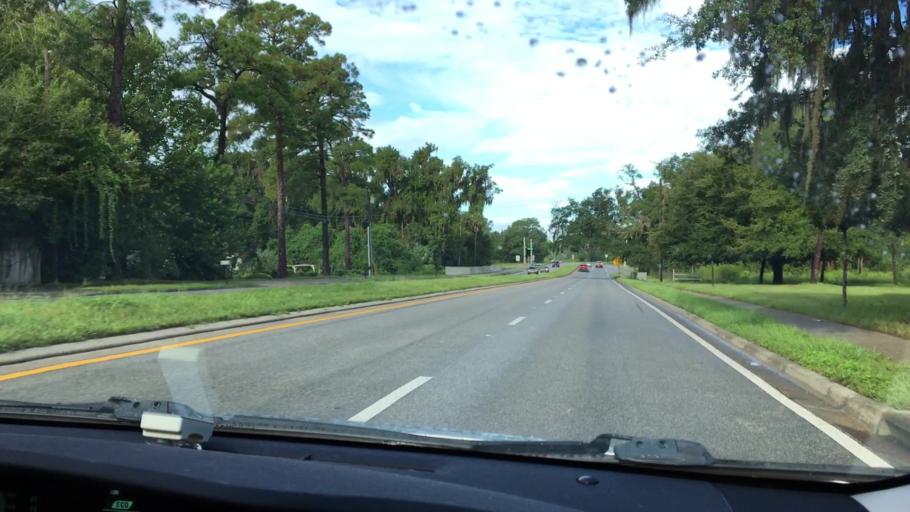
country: US
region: Florida
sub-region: Volusia County
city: Deltona
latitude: 28.8747
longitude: -81.2681
